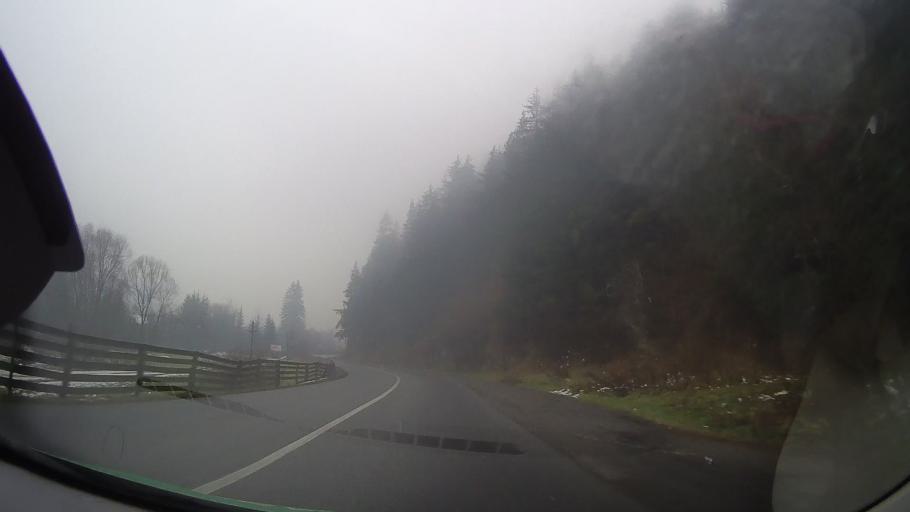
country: RO
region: Harghita
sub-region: Municipiul Gheorgheni
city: Gheorgheni
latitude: 46.7368
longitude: 25.6569
